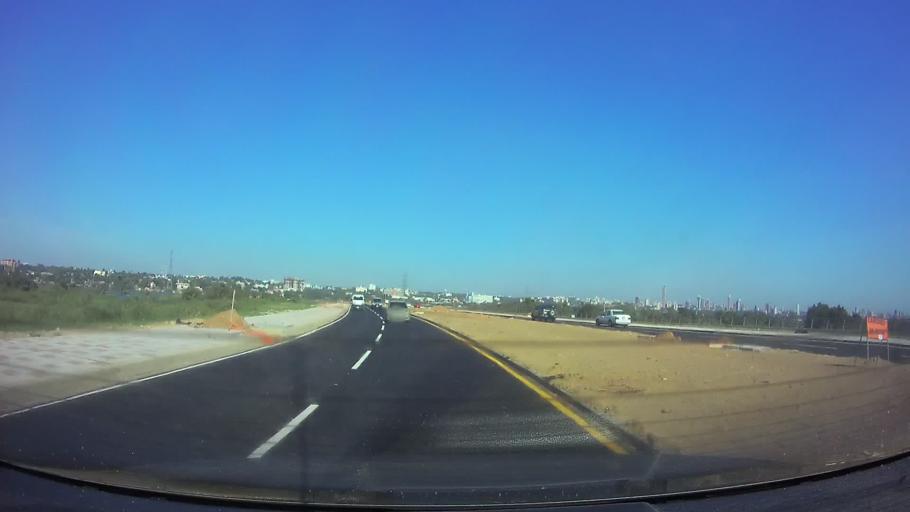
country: PY
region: Asuncion
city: Asuncion
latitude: -25.2577
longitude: -57.6080
